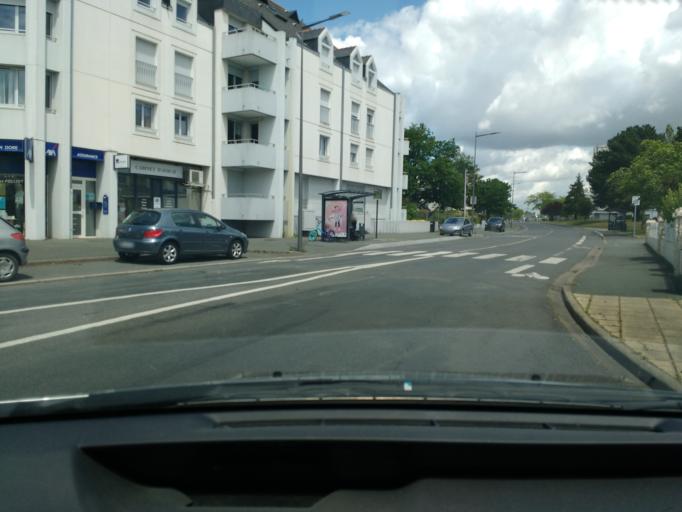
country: FR
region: Pays de la Loire
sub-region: Departement de Maine-et-Loire
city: Trelaze
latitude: 47.4680
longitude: -0.4933
